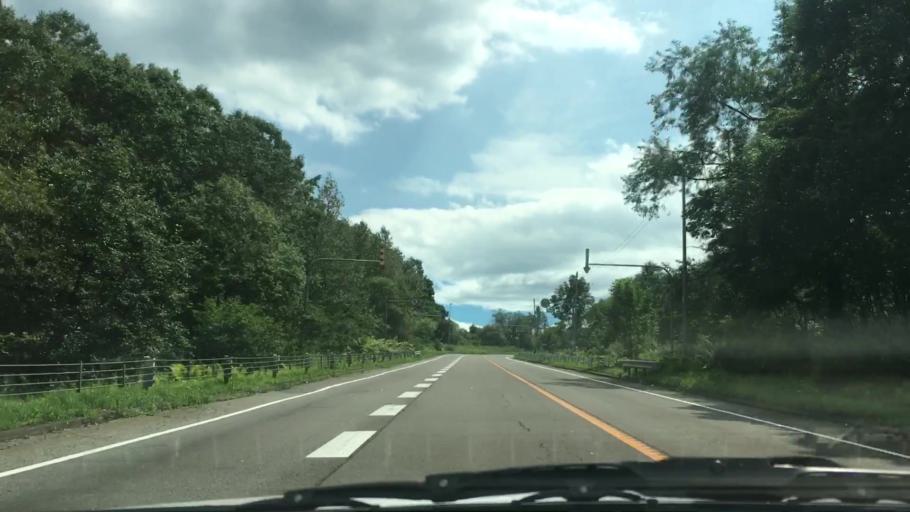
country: JP
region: Hokkaido
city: Otofuke
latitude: 43.2796
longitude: 143.4065
